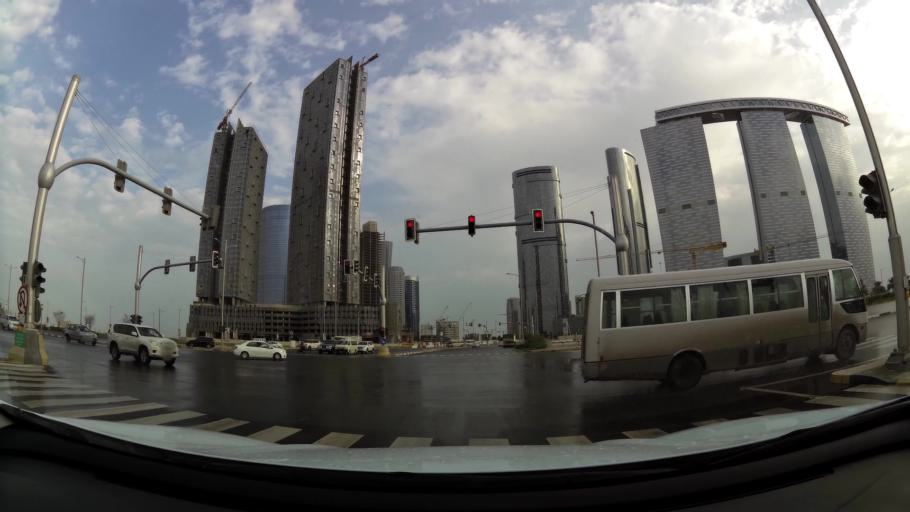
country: AE
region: Abu Dhabi
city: Abu Dhabi
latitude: 24.4913
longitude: 54.4041
